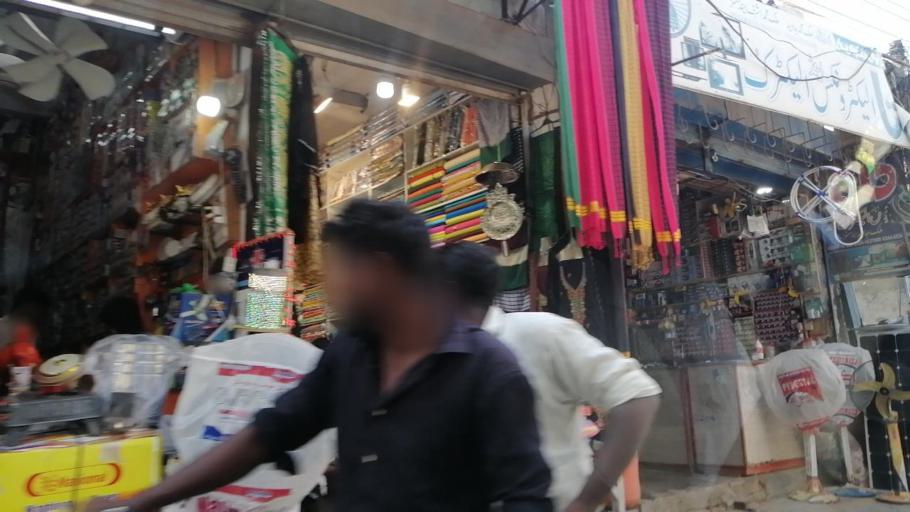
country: PK
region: Punjab
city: Kamalia
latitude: 30.7273
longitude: 72.6561
